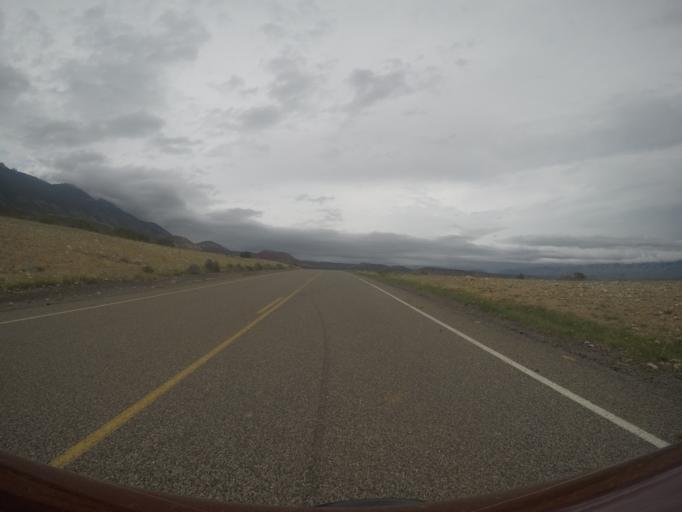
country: US
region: Wyoming
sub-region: Big Horn County
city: Lovell
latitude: 45.0927
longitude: -108.2502
